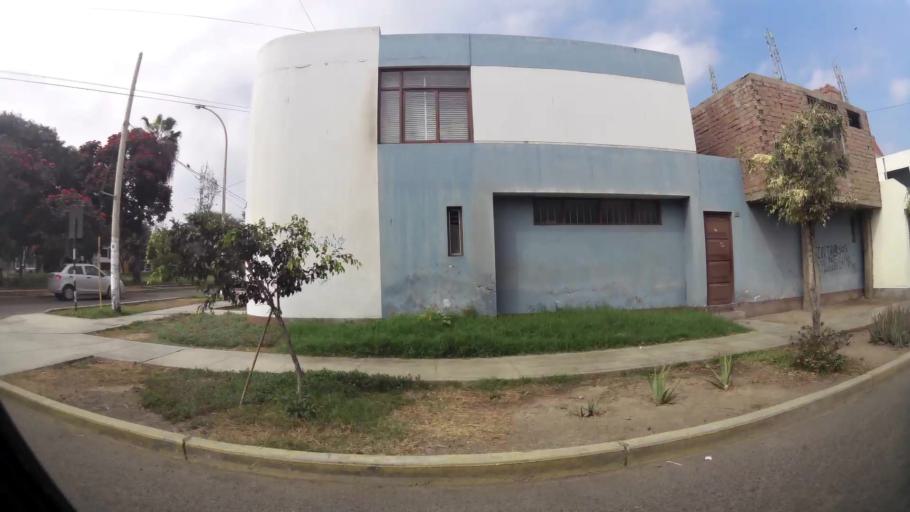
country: PE
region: La Libertad
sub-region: Provincia de Trujillo
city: Trujillo
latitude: -8.1179
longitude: -79.0216
